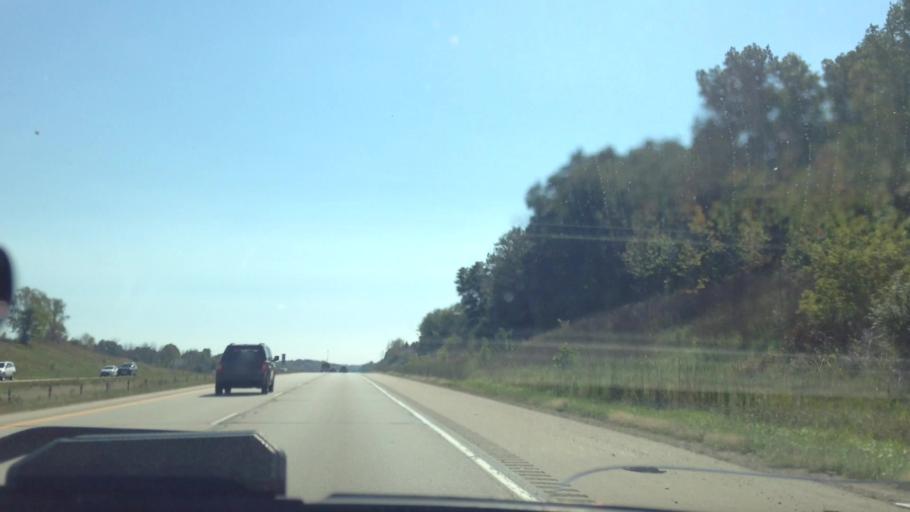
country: US
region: Wisconsin
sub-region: Ozaukee County
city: Grafton
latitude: 43.3064
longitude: -87.9206
